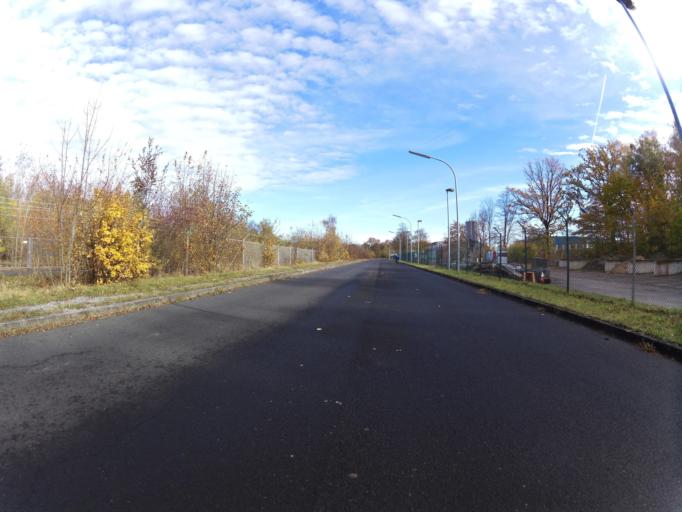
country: DE
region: Bavaria
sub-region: Regierungsbezirk Unterfranken
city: Giebelstadt
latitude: 49.6578
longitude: 9.9726
